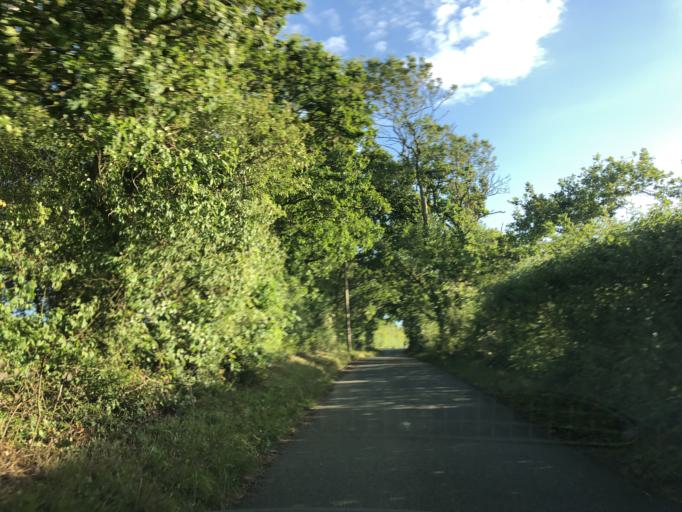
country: GB
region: England
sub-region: Isle of Wight
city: Yarmouth
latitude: 50.7022
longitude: -1.4691
